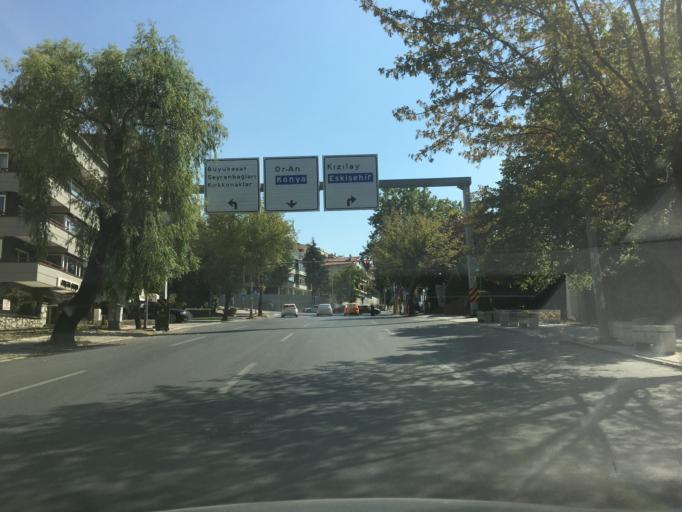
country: TR
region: Ankara
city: Cankaya
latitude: 39.8941
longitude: 32.8686
